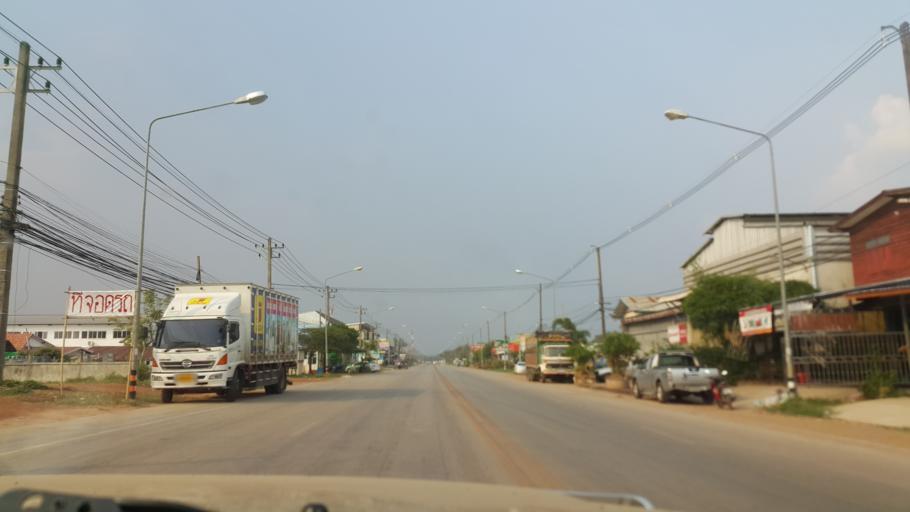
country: TH
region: Nakhon Phanom
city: That Phanom
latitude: 16.9454
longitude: 104.7211
